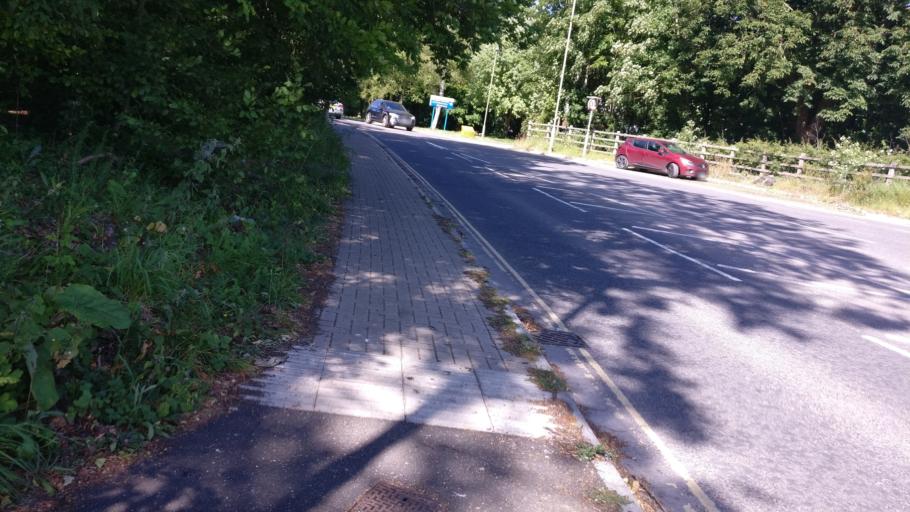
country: GB
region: England
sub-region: Hampshire
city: Basingstoke
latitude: 51.2829
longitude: -1.1093
